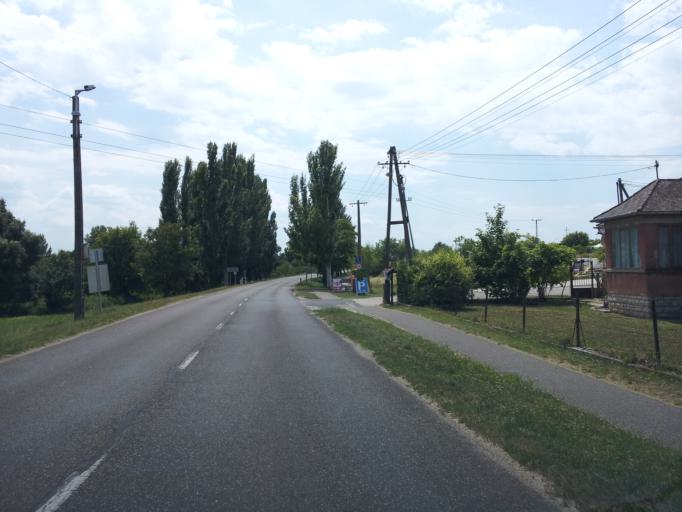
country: HU
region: Veszprem
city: Tihany
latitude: 46.9124
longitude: 17.8156
